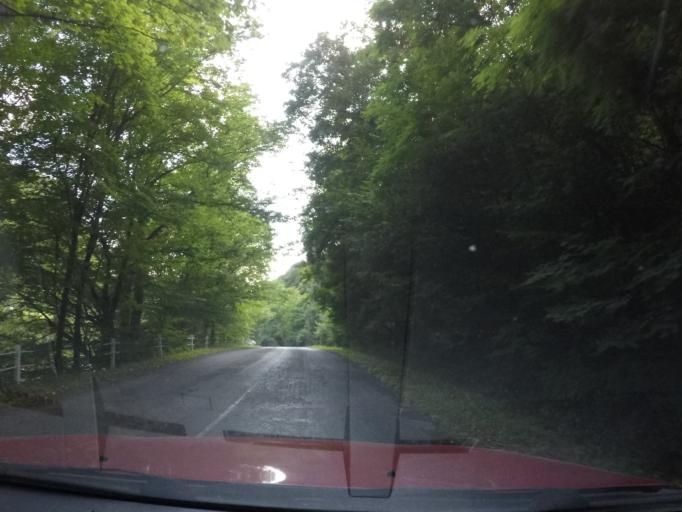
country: UA
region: Zakarpattia
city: Velykyi Bereznyi
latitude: 48.9458
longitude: 22.4956
